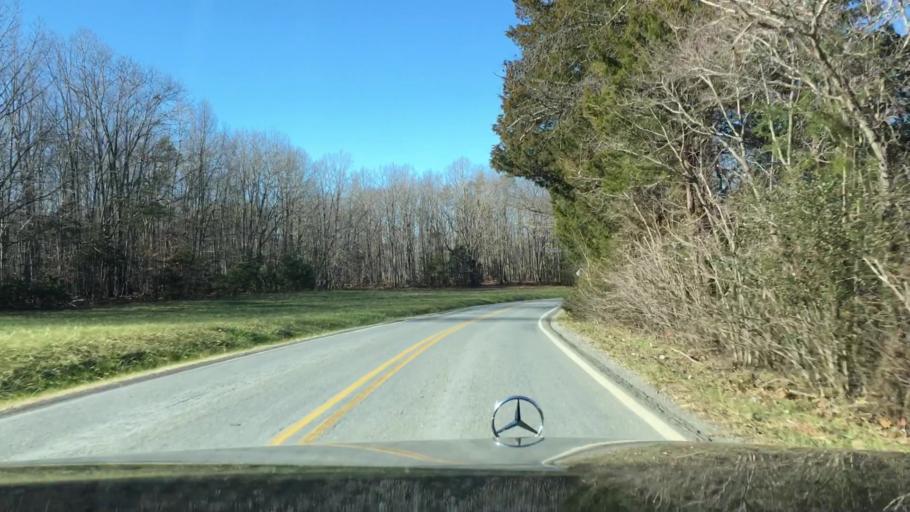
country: US
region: Virginia
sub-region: Pittsylvania County
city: Motley
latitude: 37.1835
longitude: -79.4159
